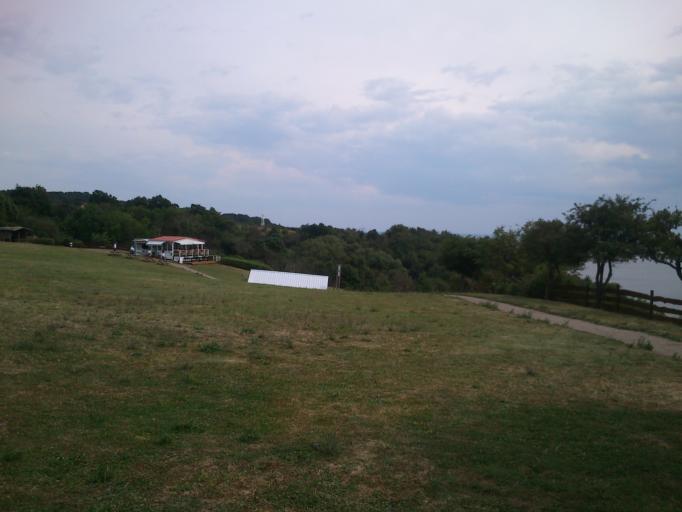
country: PL
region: West Pomeranian Voivodeship
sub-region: Powiat kamienski
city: Miedzyzdroje
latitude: 53.8650
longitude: 14.4297
